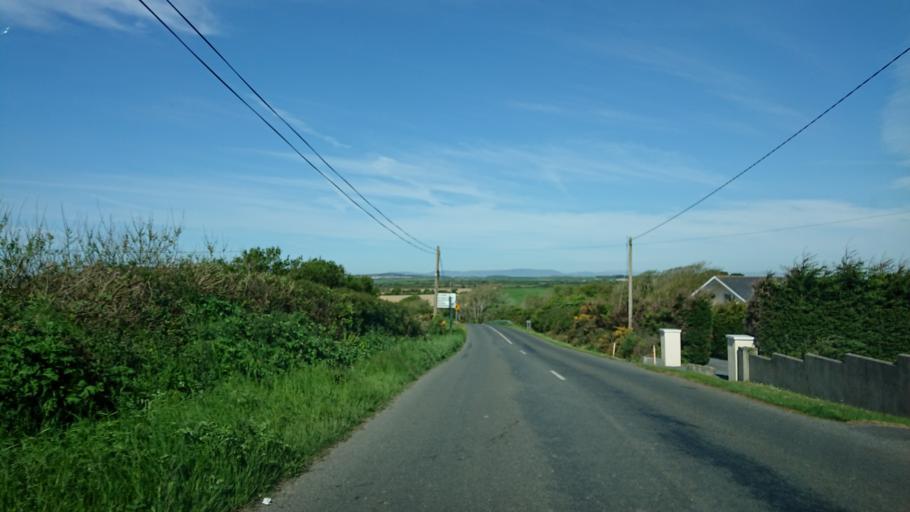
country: IE
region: Munster
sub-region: Waterford
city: Dunmore East
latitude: 52.1704
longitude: -7.0661
